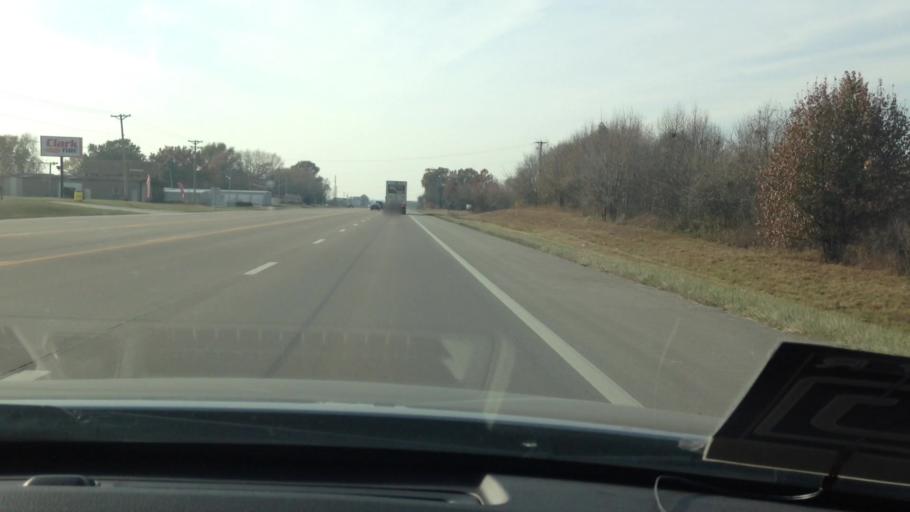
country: US
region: Missouri
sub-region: Henry County
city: Clinton
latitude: 38.3894
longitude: -93.8003
